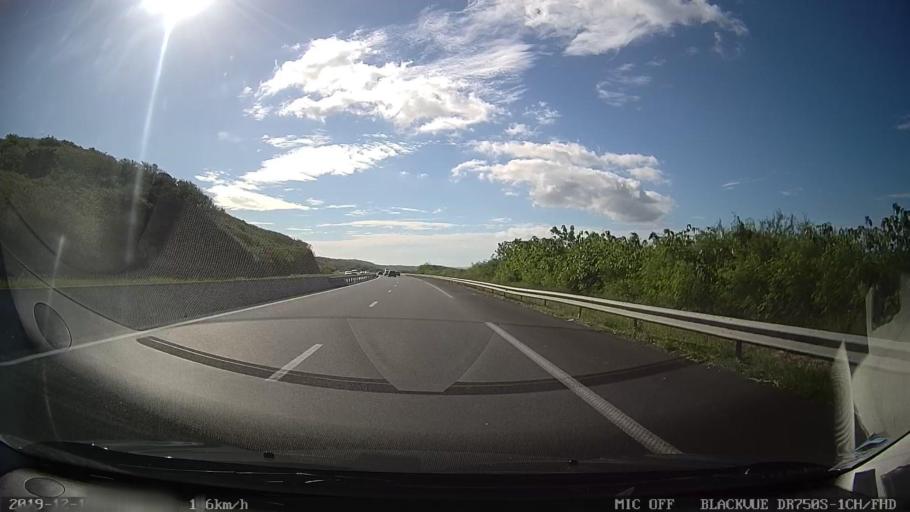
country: RE
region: Reunion
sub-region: Reunion
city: Les Avirons
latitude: -21.2421
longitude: 55.3181
